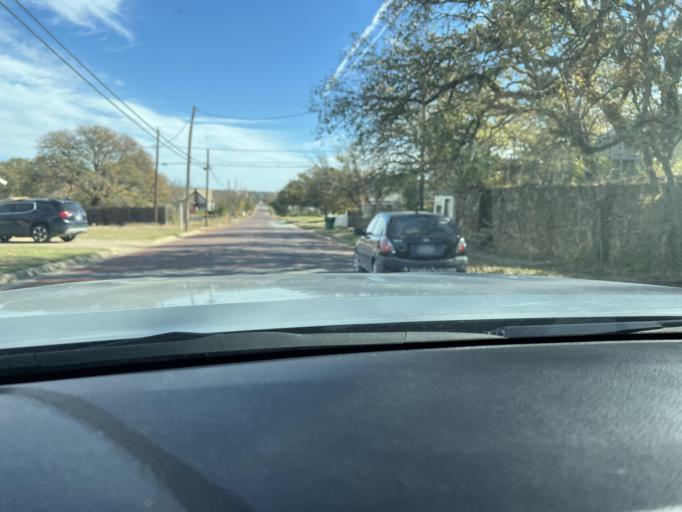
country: US
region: Texas
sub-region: Eastland County
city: Eastland
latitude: 32.3995
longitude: -98.8267
